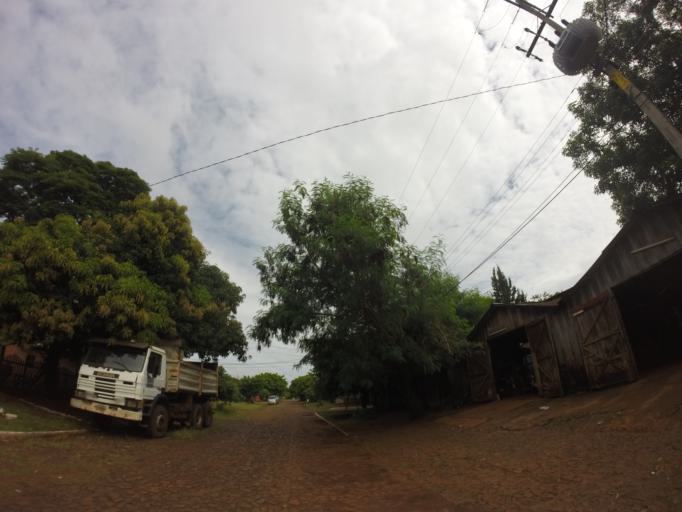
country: PY
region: Alto Parana
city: Ciudad del Este
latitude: -25.4090
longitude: -54.6446
